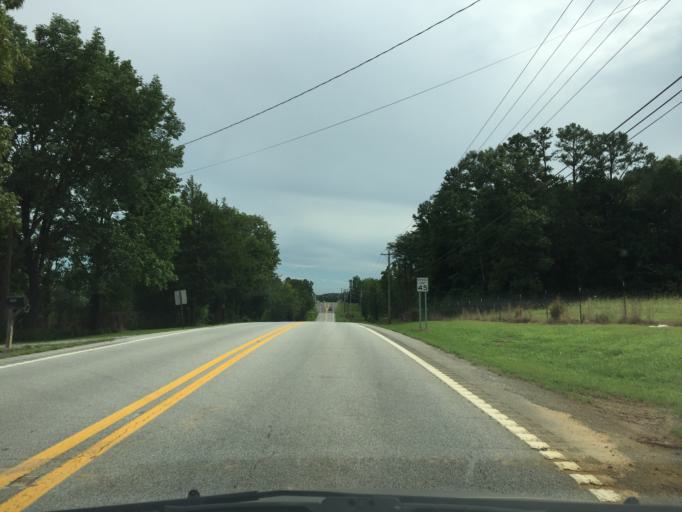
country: US
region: Tennessee
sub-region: Bradley County
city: Hopewell
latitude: 35.2967
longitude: -84.9631
